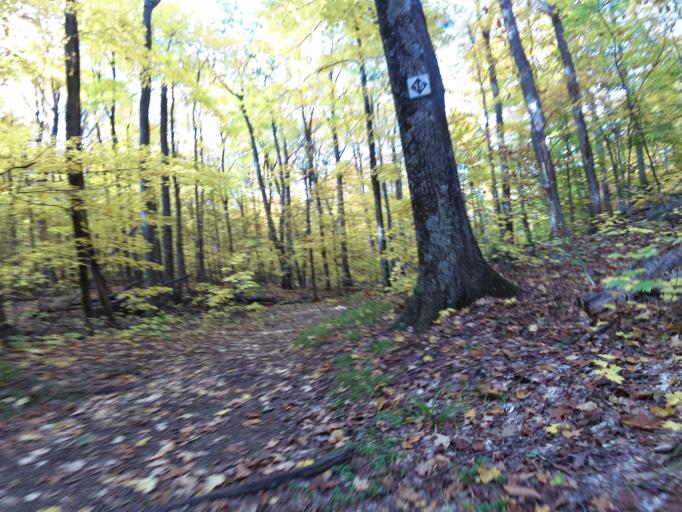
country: CA
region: Quebec
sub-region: Outaouais
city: Gatineau
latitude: 45.4789
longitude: -75.8387
